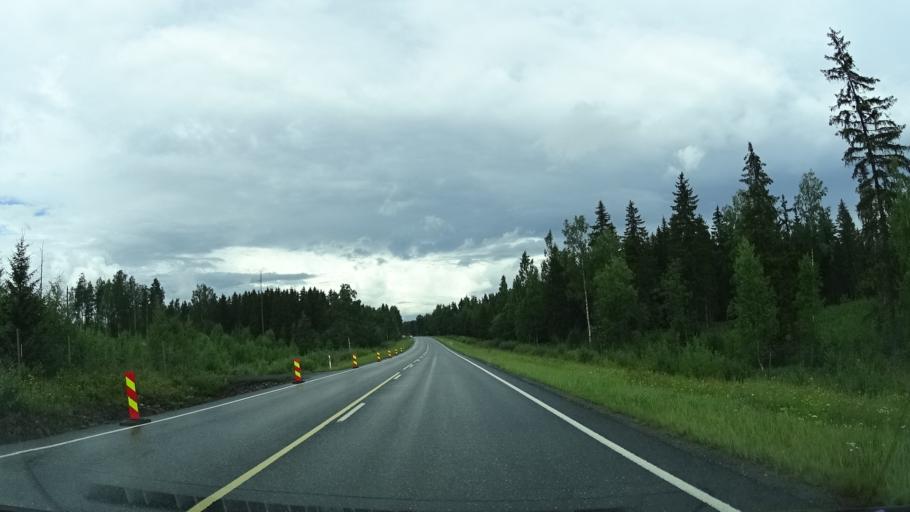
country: FI
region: Haeme
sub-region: Haemeenlinna
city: Kalvola
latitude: 61.1441
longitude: 24.0629
